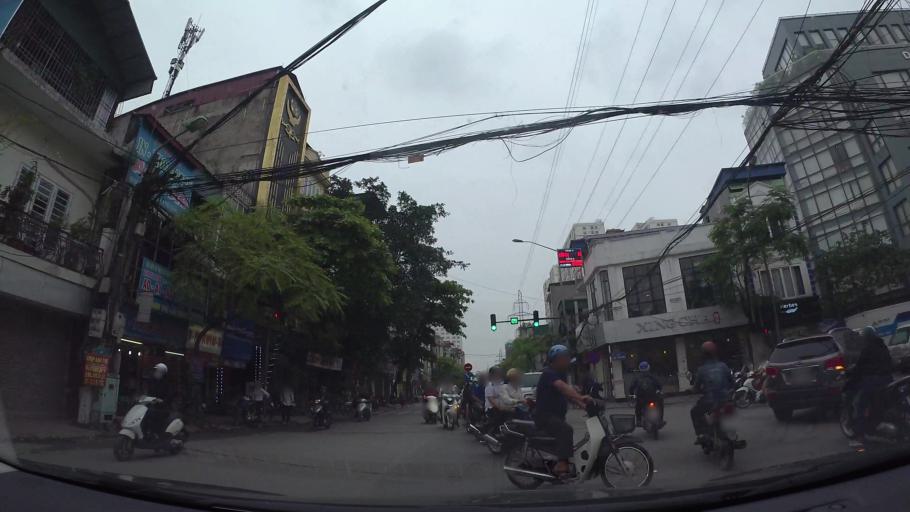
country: VN
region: Ha Noi
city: Hai BaTrung
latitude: 21.0032
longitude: 105.8697
